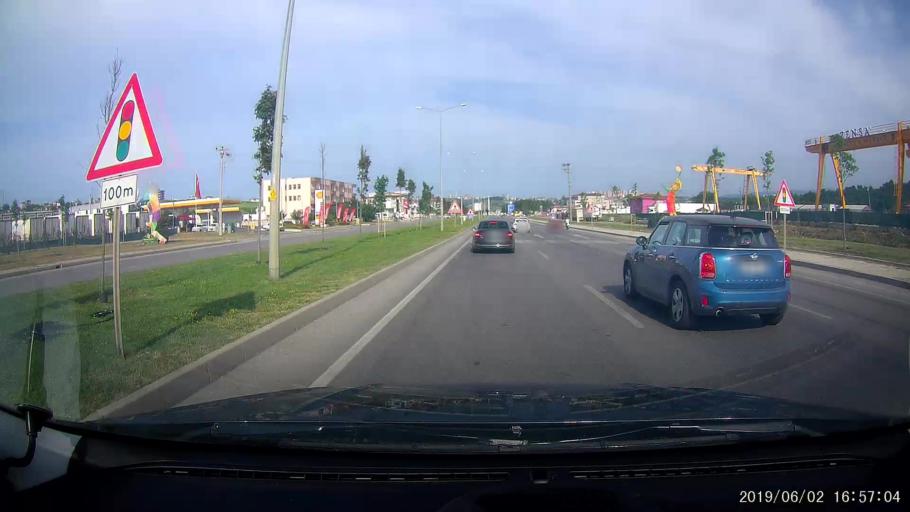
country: TR
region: Samsun
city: Samsun
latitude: 41.2914
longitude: 36.2703
